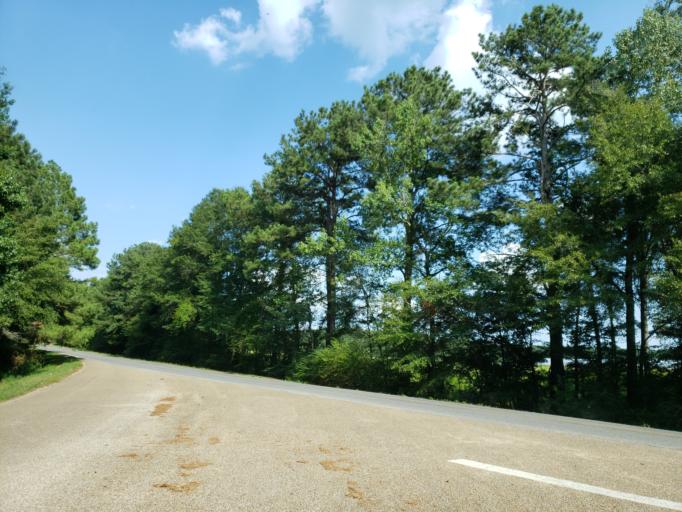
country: US
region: Mississippi
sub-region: Jones County
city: Sharon
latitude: 31.9198
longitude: -89.0383
